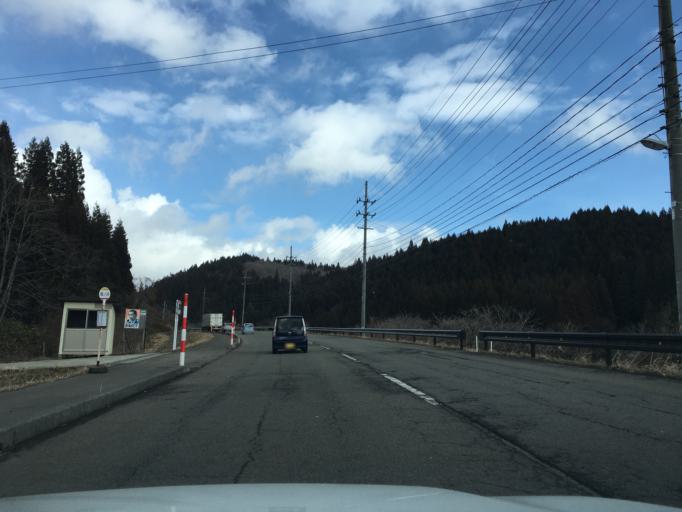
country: JP
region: Akita
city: Takanosu
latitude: 40.0927
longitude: 140.3399
